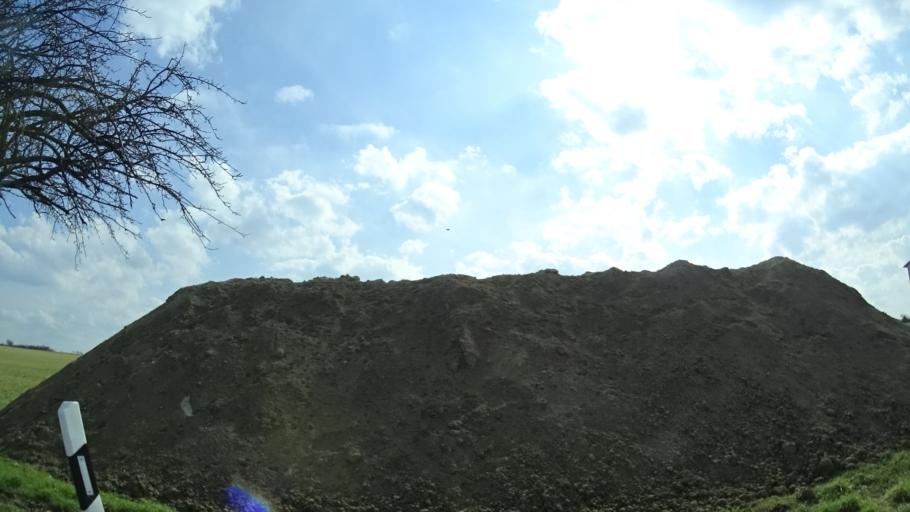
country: DE
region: Saxony-Anhalt
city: Leissling
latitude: 51.1569
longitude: 11.9007
